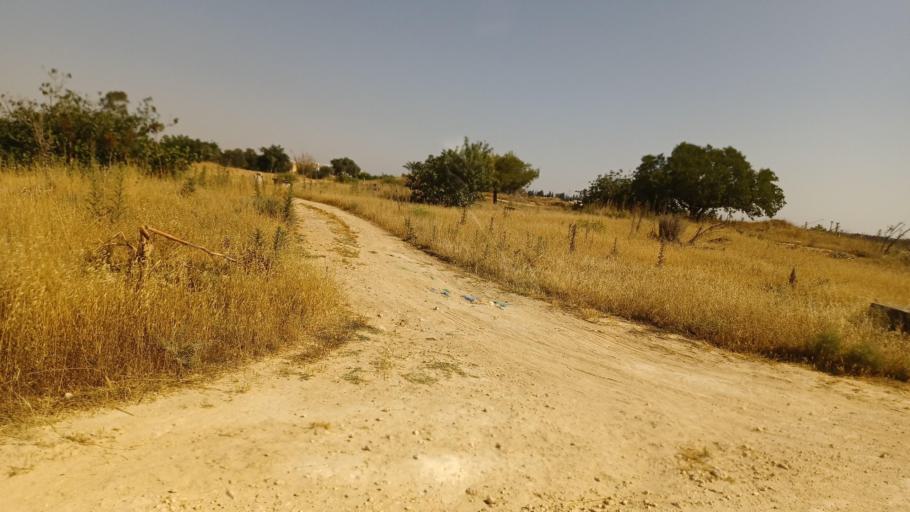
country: CY
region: Ammochostos
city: Frenaros
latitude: 35.0454
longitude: 33.9387
